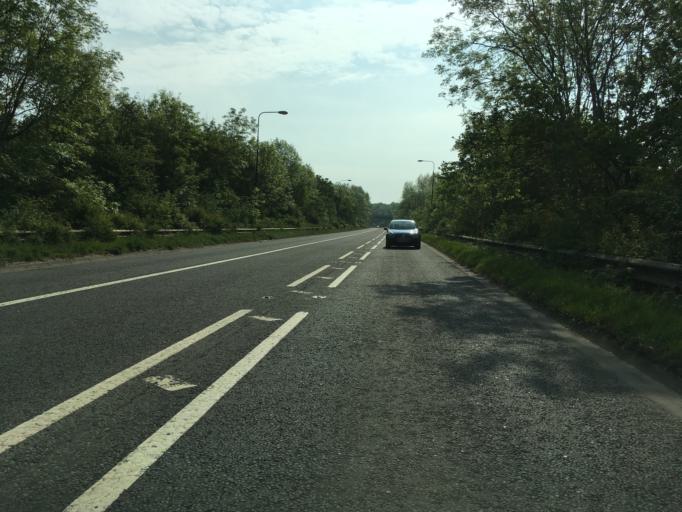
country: GB
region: England
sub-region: North Somerset
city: Long Ashton
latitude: 51.4192
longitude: -2.6775
